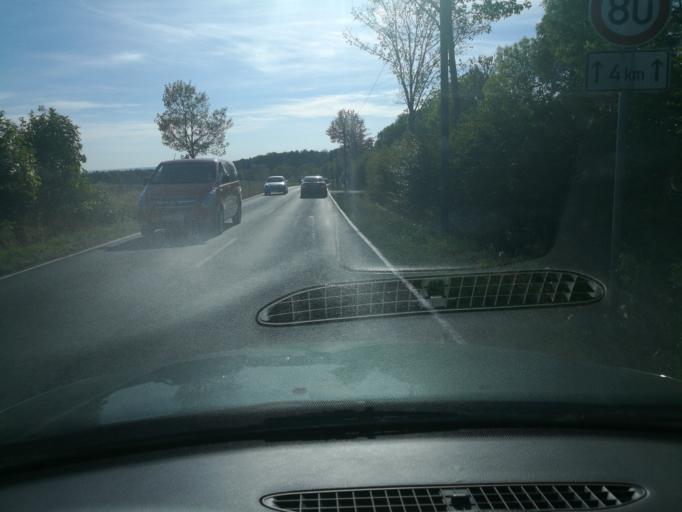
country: DE
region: Bavaria
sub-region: Regierungsbezirk Mittelfranken
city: Kalchreuth
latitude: 49.5544
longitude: 11.1213
